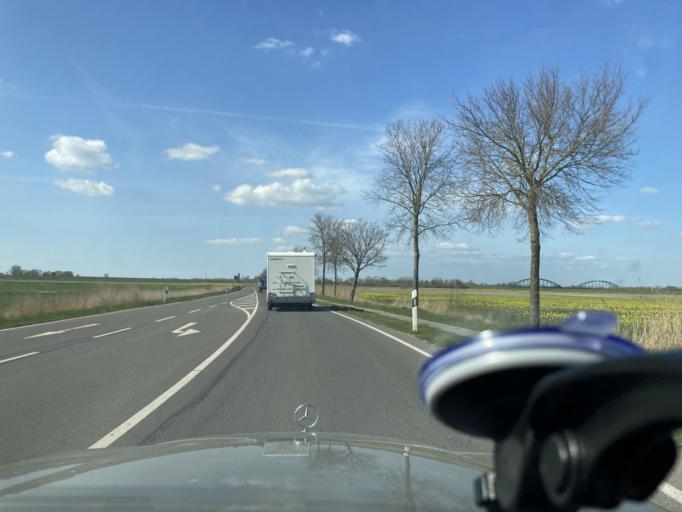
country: DE
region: Schleswig-Holstein
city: Sankt Annen
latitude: 54.3590
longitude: 9.0949
